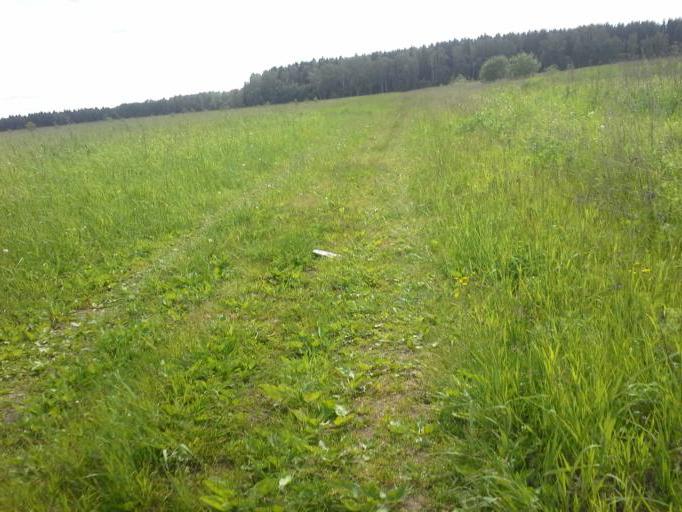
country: RU
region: Moskovskaya
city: Filimonki
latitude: 55.5593
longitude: 37.3965
